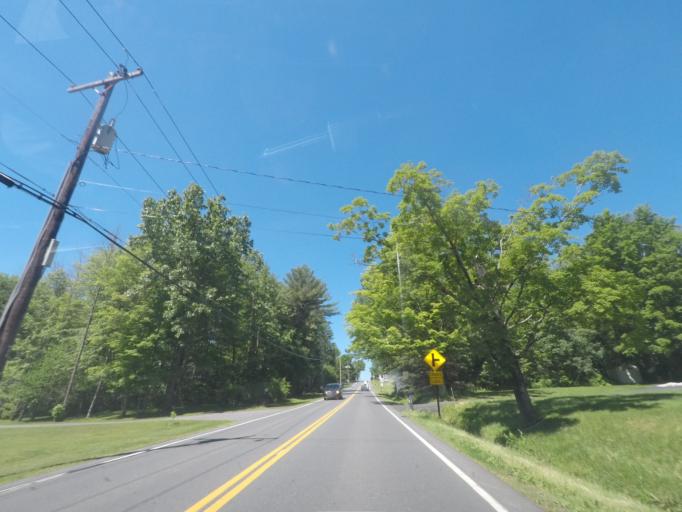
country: US
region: New York
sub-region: Saratoga County
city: Country Knolls
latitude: 42.8578
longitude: -73.8286
